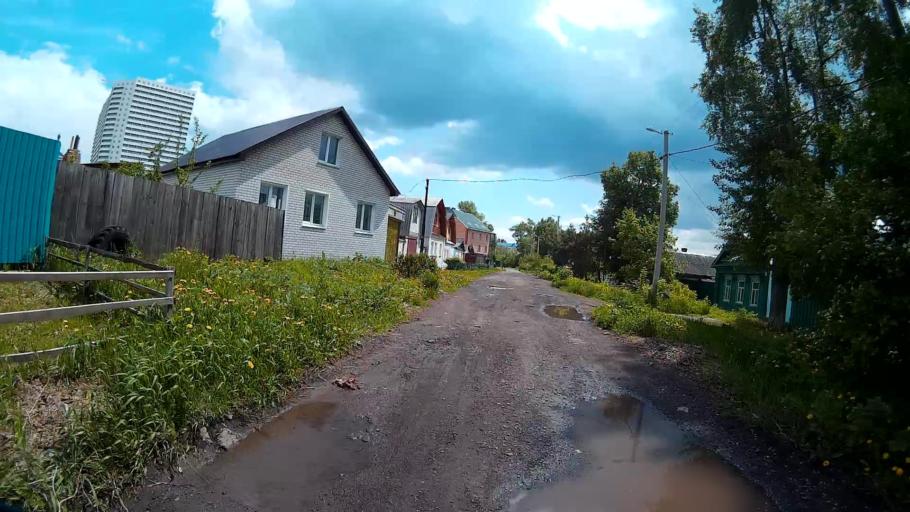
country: RU
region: Ulyanovsk
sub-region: Ulyanovskiy Rayon
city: Ulyanovsk
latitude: 54.3367
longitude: 48.3838
